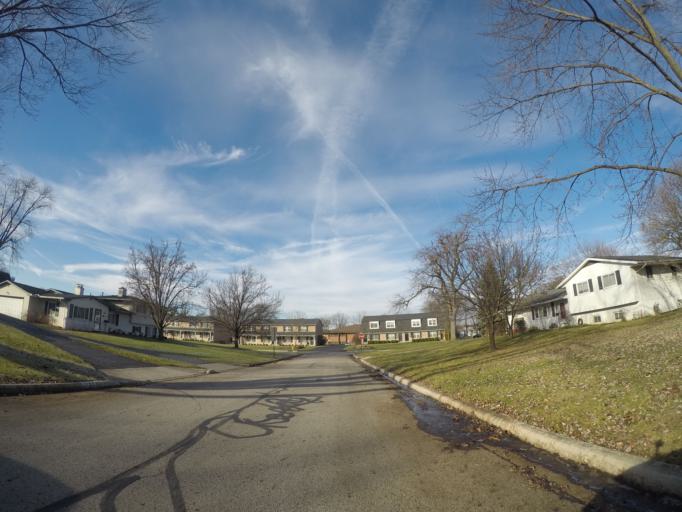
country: US
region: Ohio
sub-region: Franklin County
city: Upper Arlington
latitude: 40.0251
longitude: -83.0894
